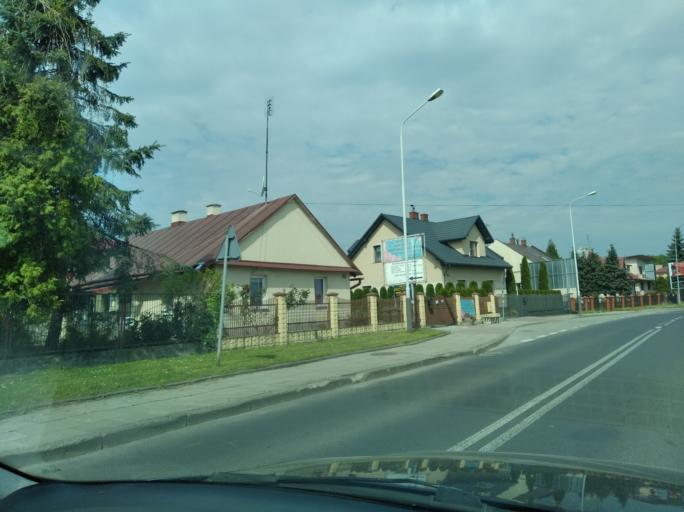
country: PL
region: Subcarpathian Voivodeship
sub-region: Powiat jaroslawski
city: Jaroslaw
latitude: 50.0286
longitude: 22.6718
